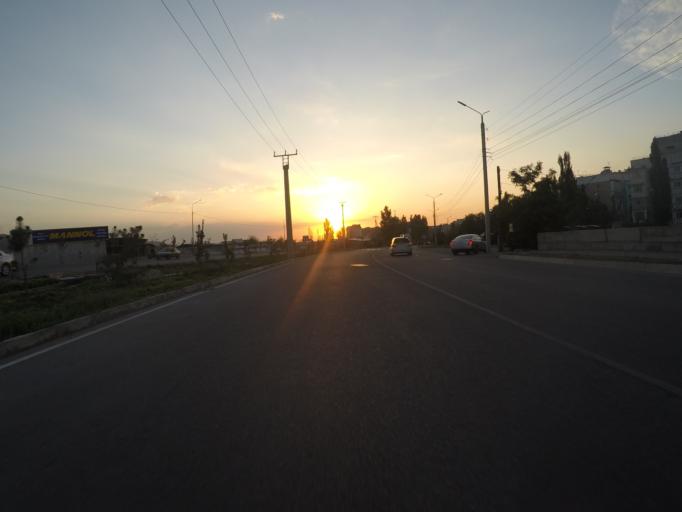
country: KG
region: Chuy
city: Bishkek
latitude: 42.8109
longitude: 74.6355
